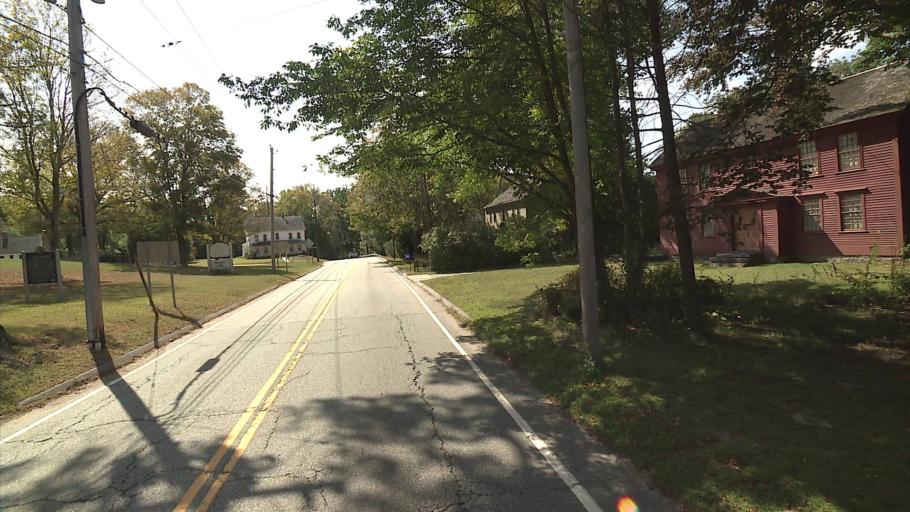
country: US
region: Connecticut
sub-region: Windham County
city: Plainfield Village
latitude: 41.6979
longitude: -71.9714
